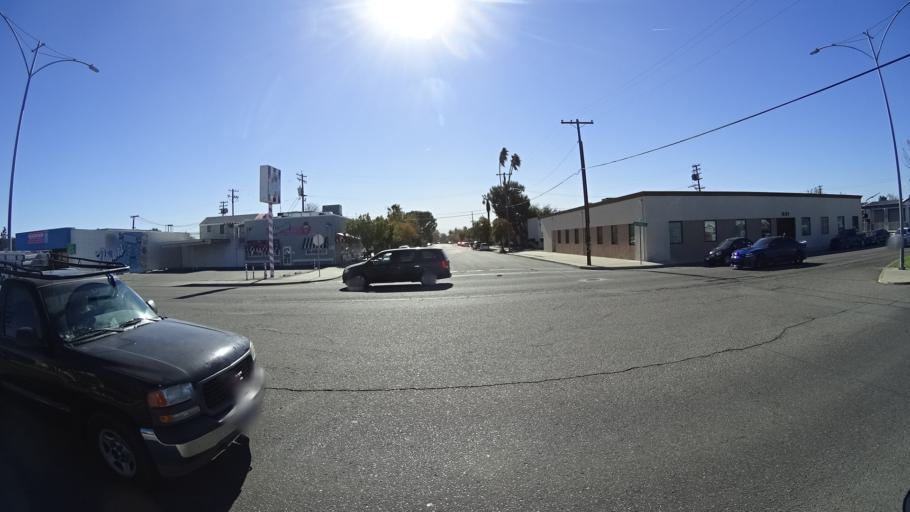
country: US
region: California
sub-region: Kern County
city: Bakersfield
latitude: 35.3686
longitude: -119.0201
